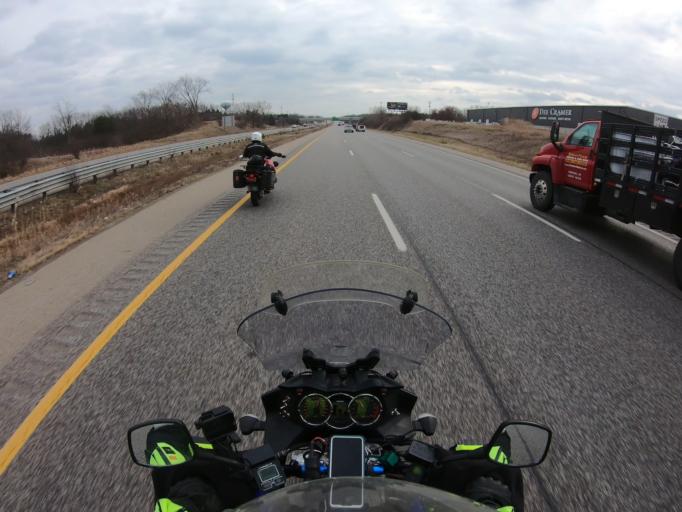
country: US
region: Michigan
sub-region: Genesee County
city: Grand Blanc
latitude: 42.8886
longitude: -83.6234
